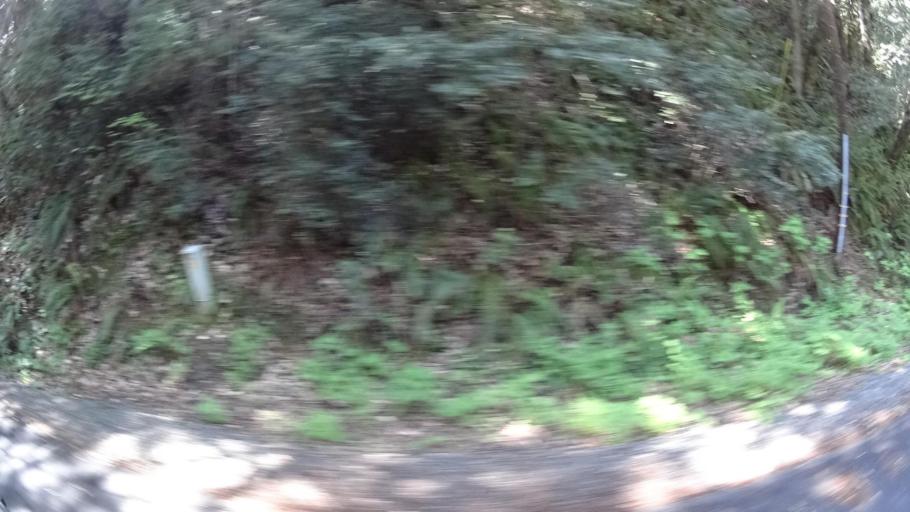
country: US
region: California
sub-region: Humboldt County
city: Rio Dell
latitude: 40.2696
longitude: -124.2047
